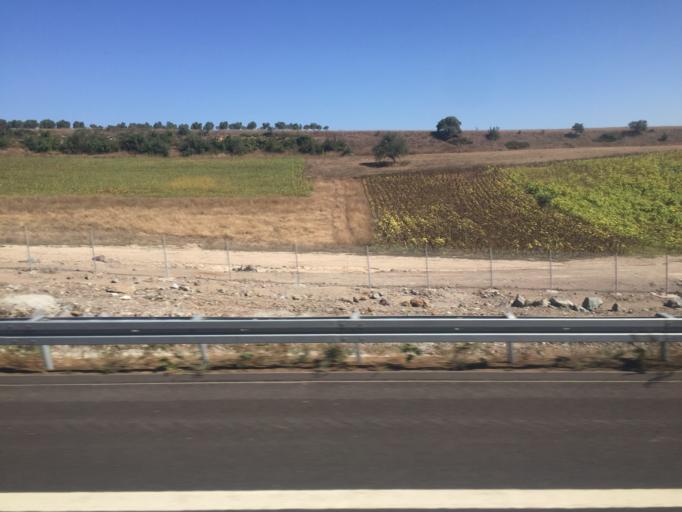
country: TR
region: Bursa
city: Mahmudiye
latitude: 40.2703
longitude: 28.6246
